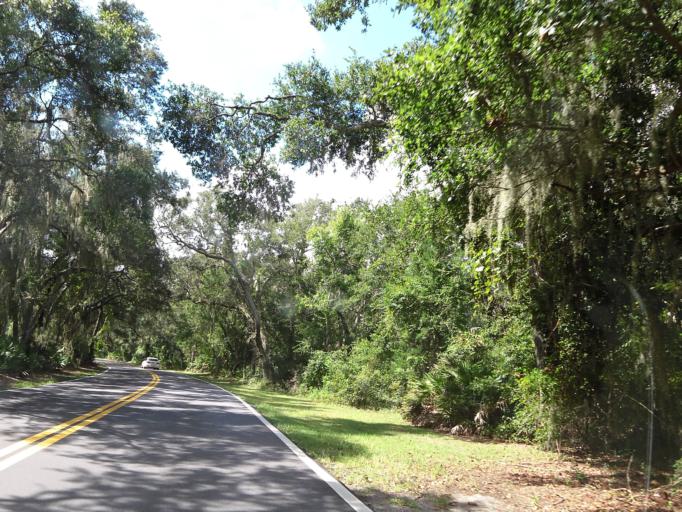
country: US
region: Florida
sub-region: Nassau County
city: Fernandina Beach
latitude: 30.5799
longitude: -81.4485
